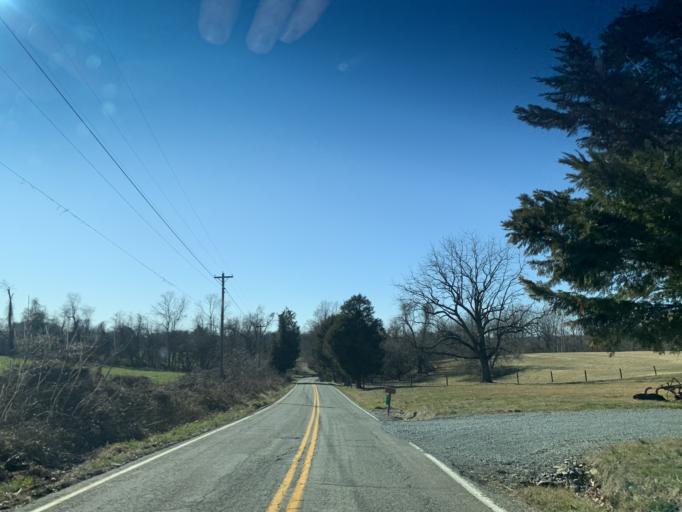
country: US
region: Maryland
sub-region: Cecil County
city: Rising Sun
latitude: 39.6870
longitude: -76.1091
